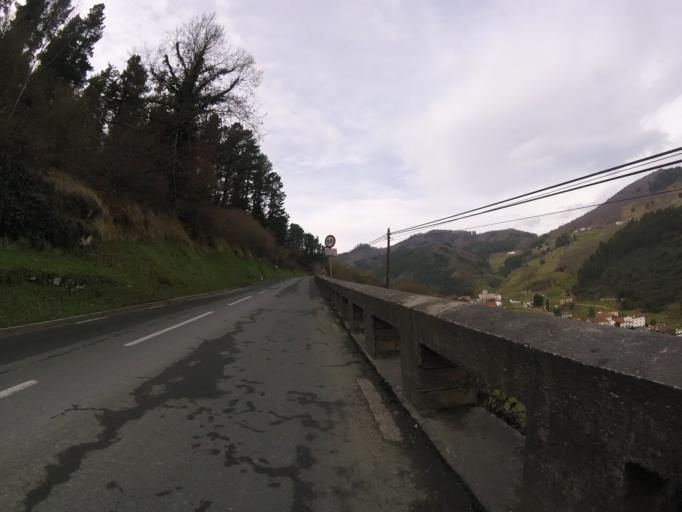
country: ES
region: Basque Country
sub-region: Provincia de Guipuzcoa
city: Albiztur
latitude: 43.1273
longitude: -2.1296
